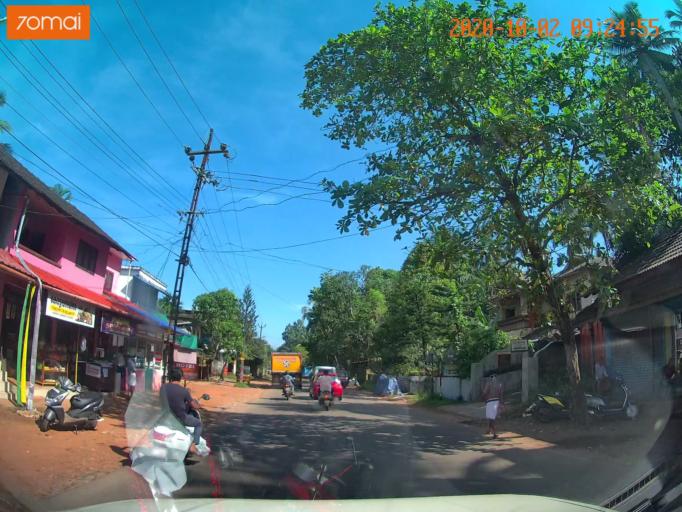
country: IN
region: Kerala
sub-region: Kozhikode
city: Naduvannur
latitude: 11.5858
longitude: 75.7660
